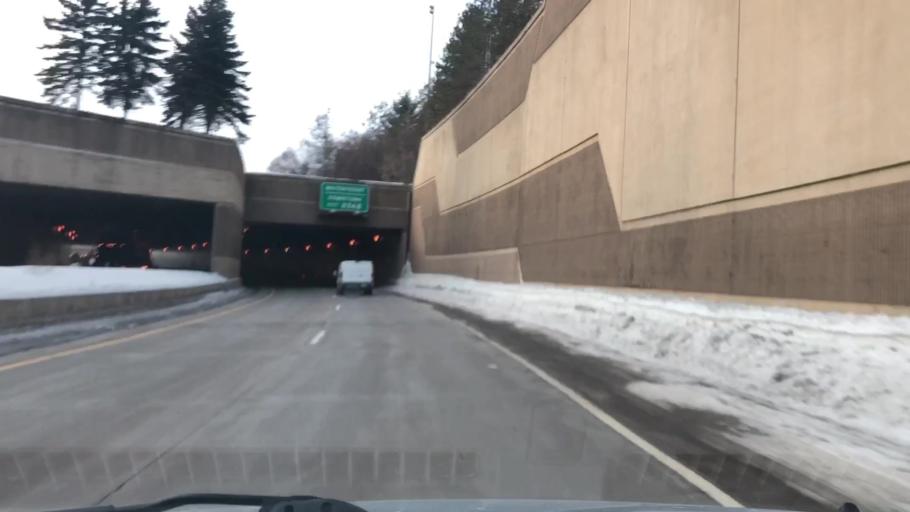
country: US
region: Minnesota
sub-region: Saint Louis County
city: Duluth
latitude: 46.7927
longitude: -92.0915
